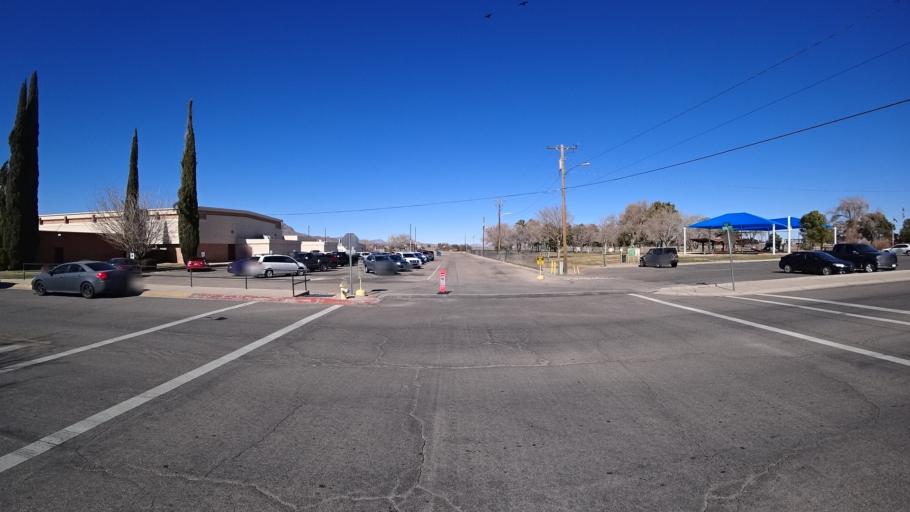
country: US
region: Arizona
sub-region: Mohave County
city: Kingman
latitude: 35.2140
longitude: -114.0313
